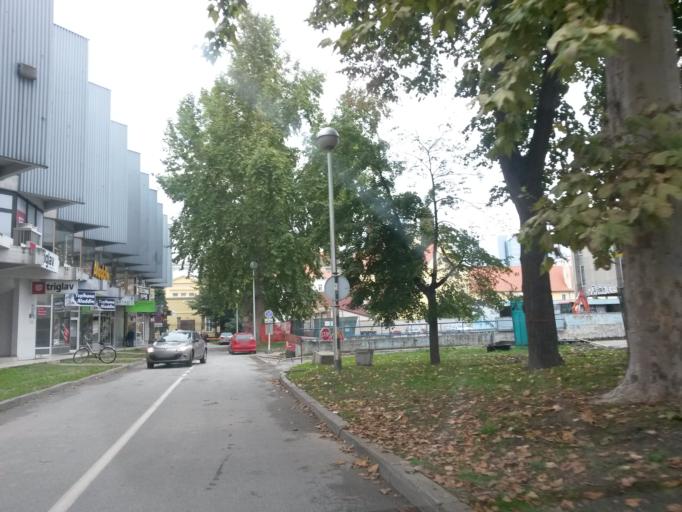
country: HR
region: Osjecko-Baranjska
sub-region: Grad Osijek
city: Osijek
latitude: 45.5598
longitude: 18.6773
